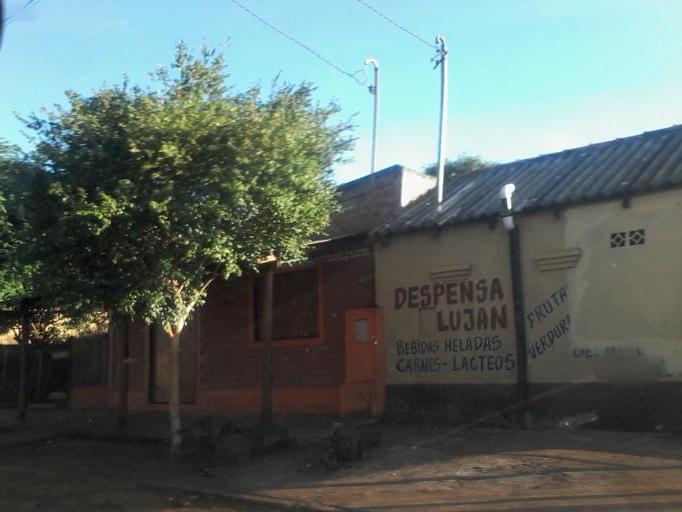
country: PY
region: Alto Parana
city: Ciudad del Este
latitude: -25.4363
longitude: -54.6399
